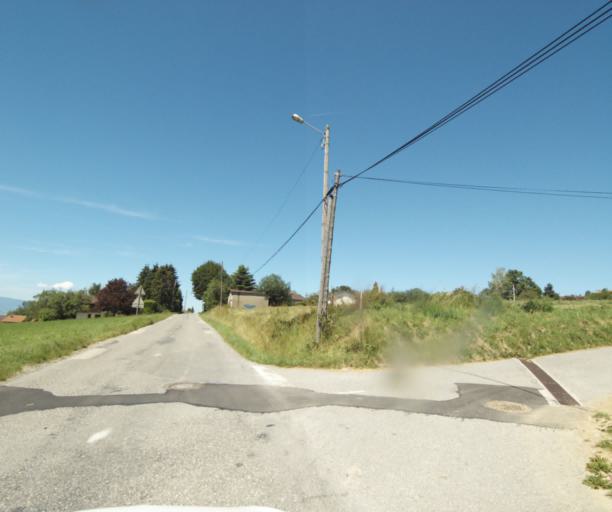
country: FR
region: Rhone-Alpes
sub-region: Departement de la Haute-Savoie
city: Loisin
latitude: 46.2789
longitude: 6.3178
